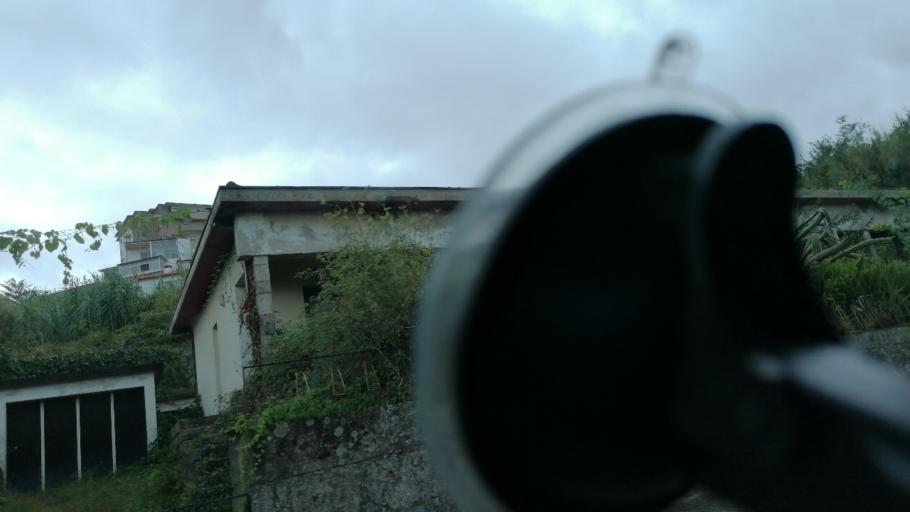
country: PT
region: Porto
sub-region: Penafiel
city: Penafiel
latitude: 41.2065
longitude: -8.2879
